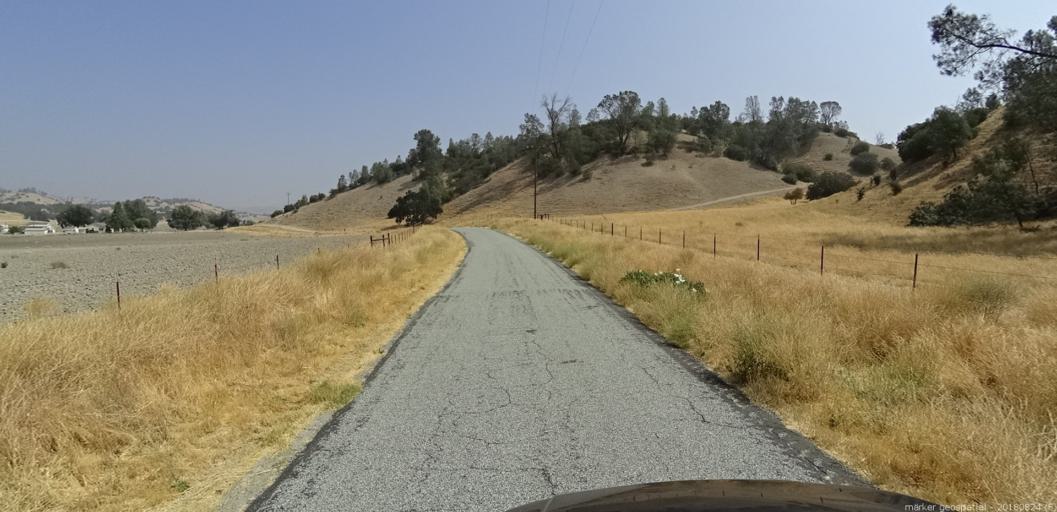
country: US
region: California
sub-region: San Luis Obispo County
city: San Miguel
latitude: 35.9526
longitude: -120.6560
